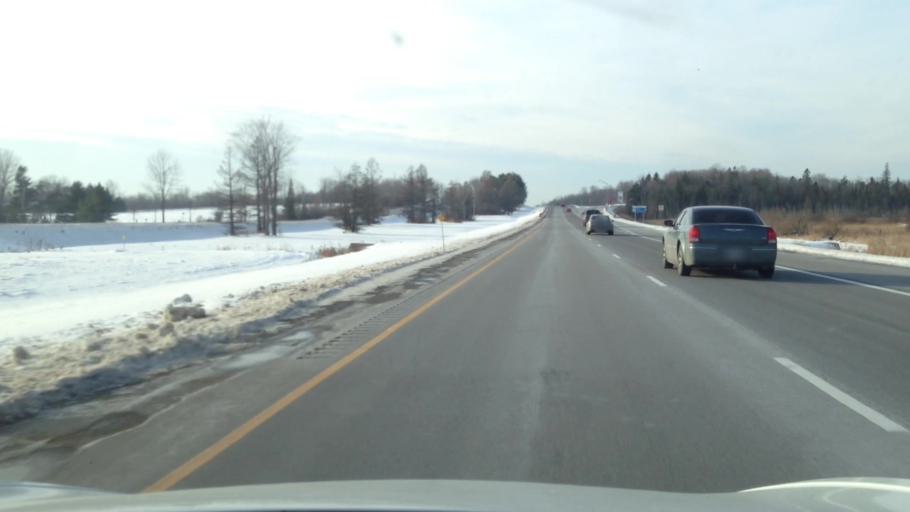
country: CA
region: Quebec
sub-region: Monteregie
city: Rigaud
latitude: 45.5455
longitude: -74.4141
